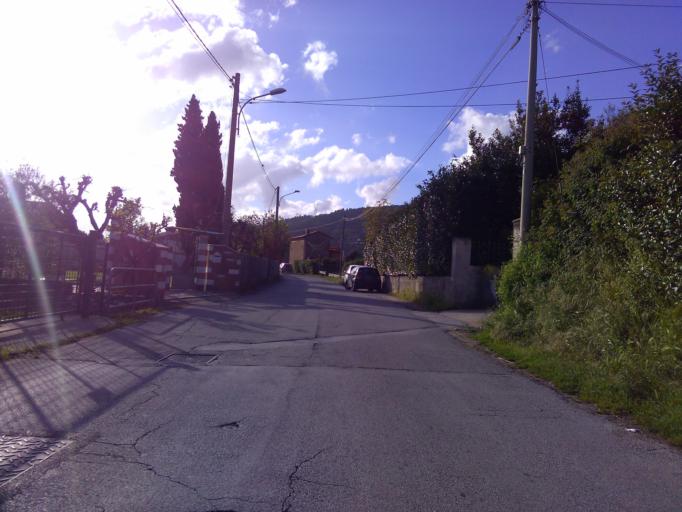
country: IT
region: Tuscany
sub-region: Provincia di Lucca
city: Ripa-Pozzi-Querceta-Ponterosso
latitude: 43.9872
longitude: 10.2025
